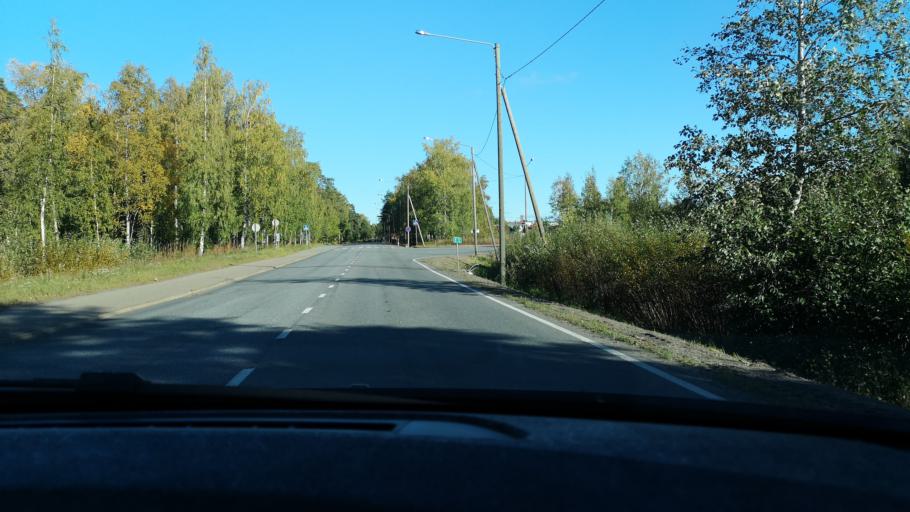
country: FI
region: Ostrobothnia
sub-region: Vaasa
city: Vaasa
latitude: 63.0892
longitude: 21.5783
